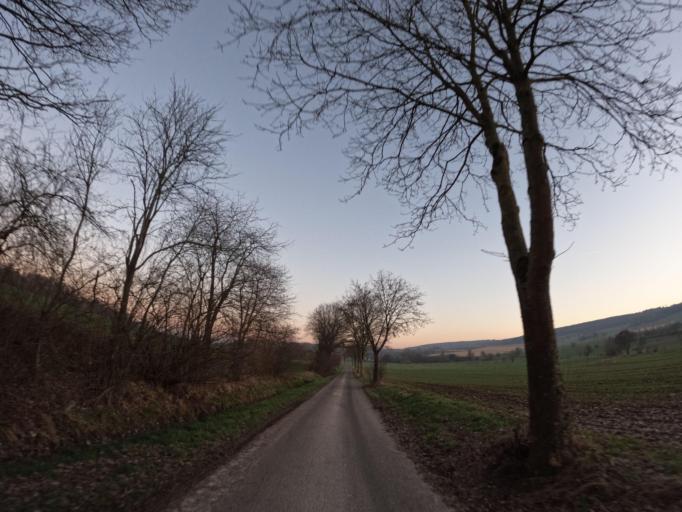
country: DE
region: Lower Saxony
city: Uslar
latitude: 51.6781
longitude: 9.5910
